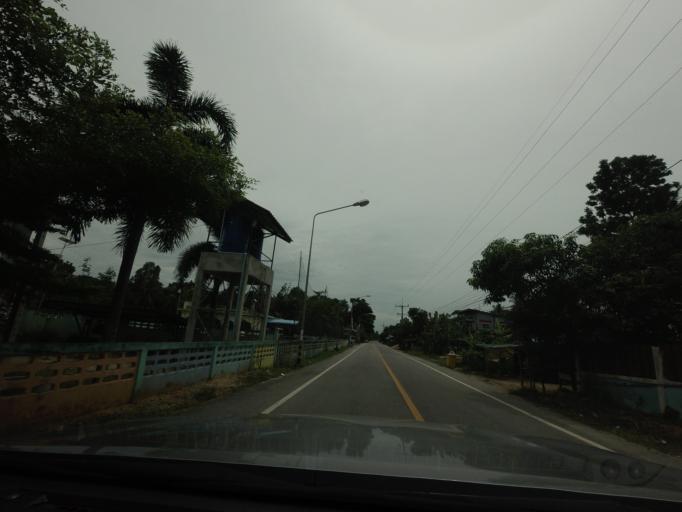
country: TH
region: Pattani
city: Kapho
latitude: 6.6144
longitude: 101.5410
